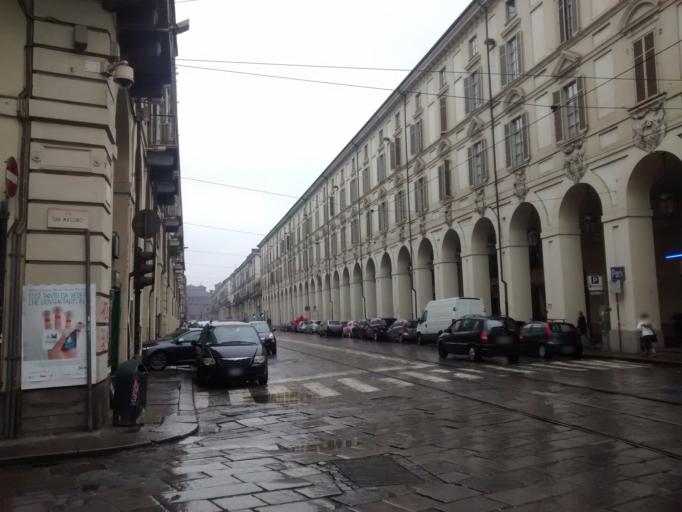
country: IT
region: Piedmont
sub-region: Provincia di Torino
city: Turin
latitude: 45.0672
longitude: 7.6915
